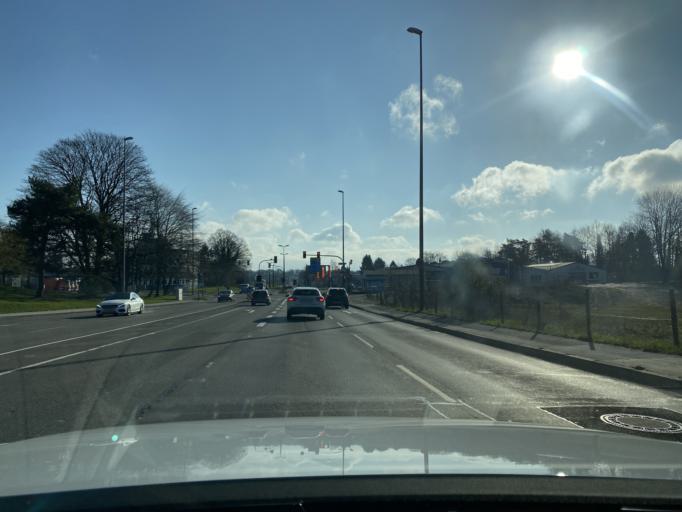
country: DE
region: North Rhine-Westphalia
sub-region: Regierungsbezirk Dusseldorf
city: Remscheid
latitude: 51.1803
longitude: 7.2304
